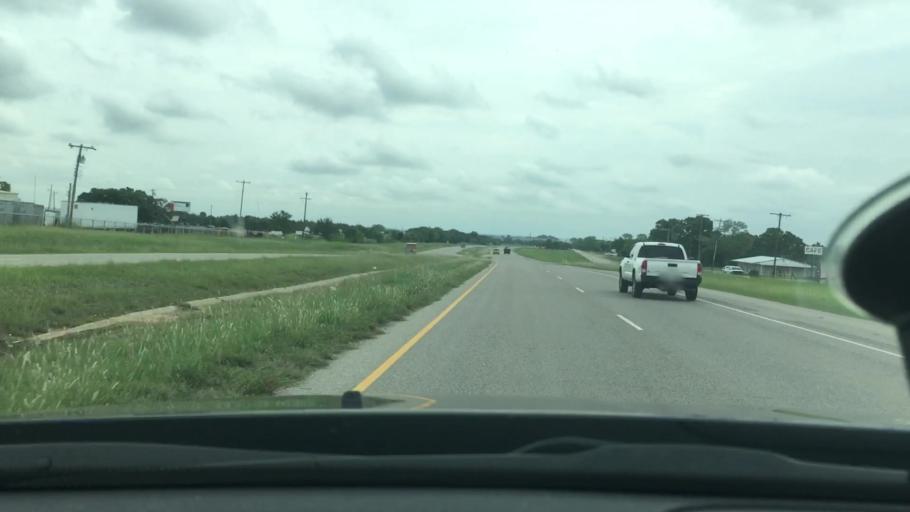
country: US
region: Oklahoma
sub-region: Carter County
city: Wilson
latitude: 34.1727
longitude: -97.4415
